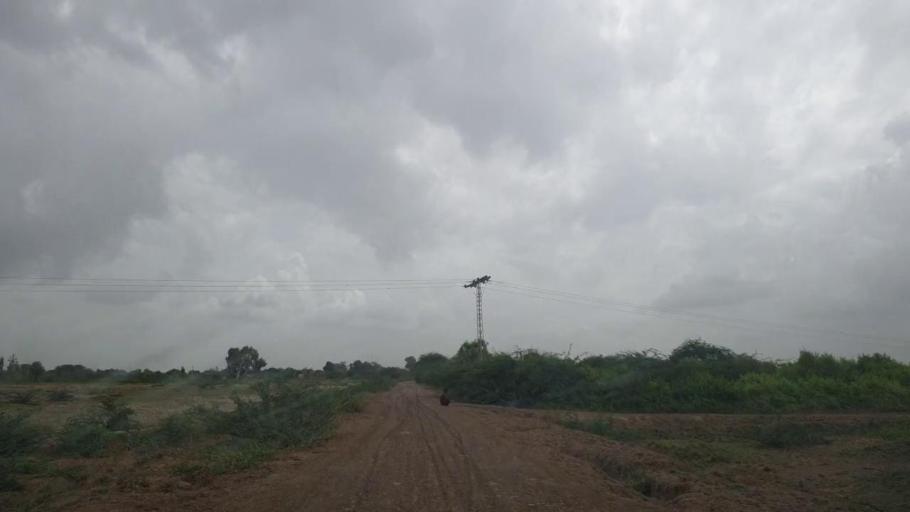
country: PK
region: Sindh
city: Naukot
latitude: 24.8786
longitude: 69.2438
